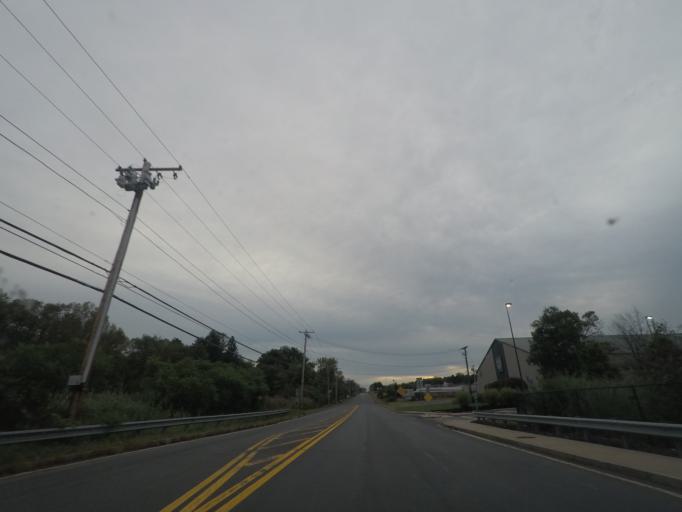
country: US
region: Massachusetts
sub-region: Hampden County
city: Ludlow
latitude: 42.1500
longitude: -72.4716
